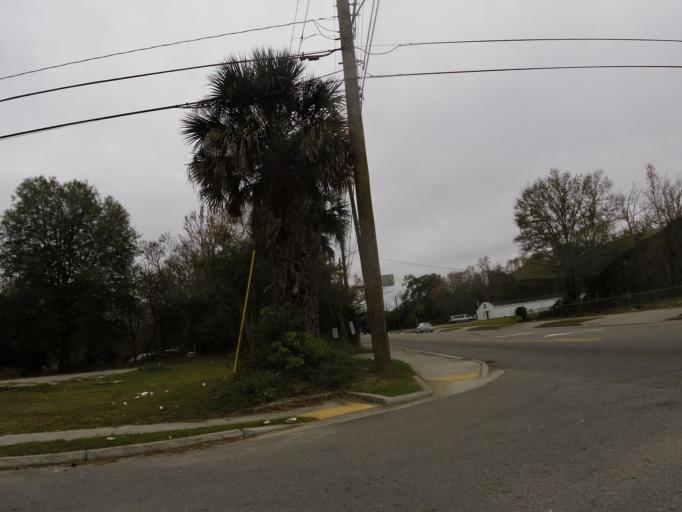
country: US
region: Florida
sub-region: Duval County
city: Jacksonville
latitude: 30.3748
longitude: -81.6990
